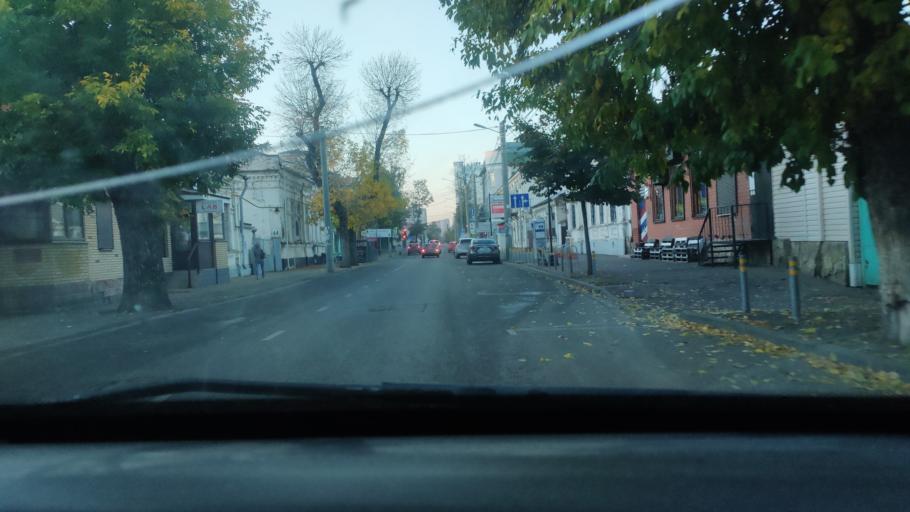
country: RU
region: Krasnodarskiy
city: Krasnodar
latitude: 45.0298
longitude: 38.9700
